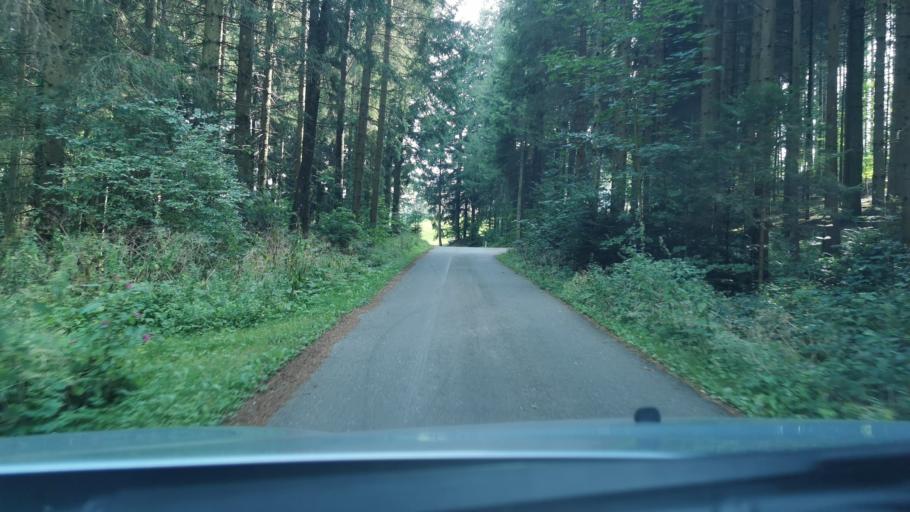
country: AT
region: Styria
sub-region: Politischer Bezirk Weiz
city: Strallegg
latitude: 47.4046
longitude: 15.6940
